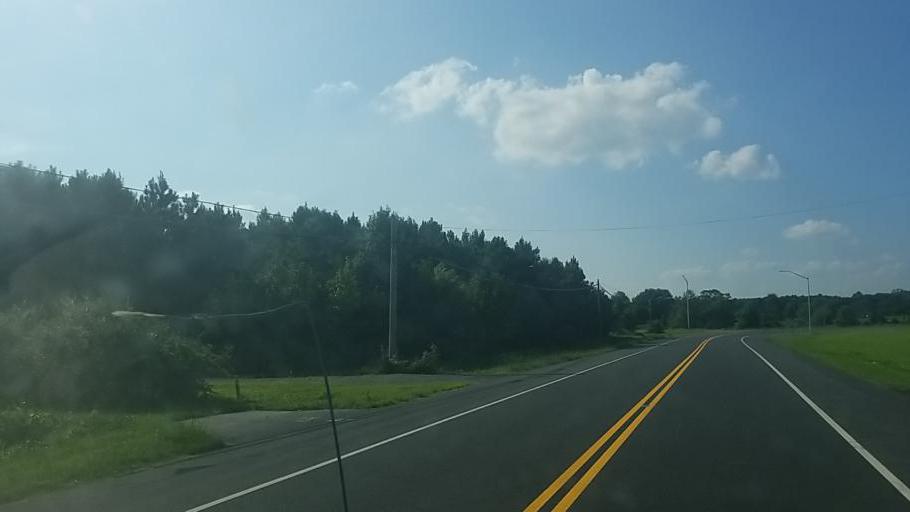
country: US
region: Maryland
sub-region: Worcester County
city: Ocean Pines
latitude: 38.3853
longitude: -75.2020
